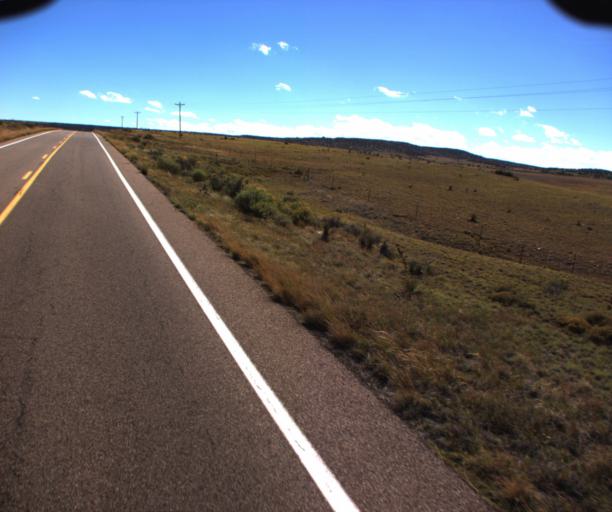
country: US
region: Arizona
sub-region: Apache County
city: Saint Johns
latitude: 34.4915
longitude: -109.6209
